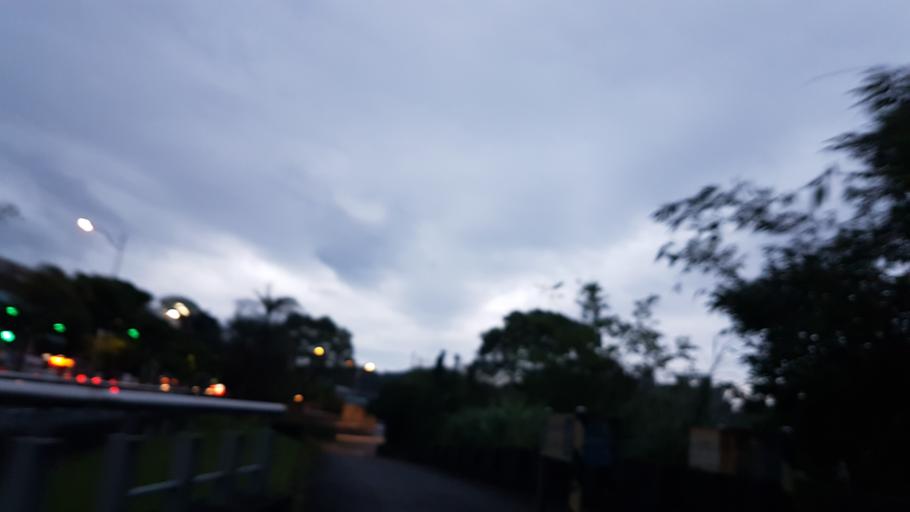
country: TW
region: Taipei
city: Taipei
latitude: 24.9993
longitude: 121.5805
